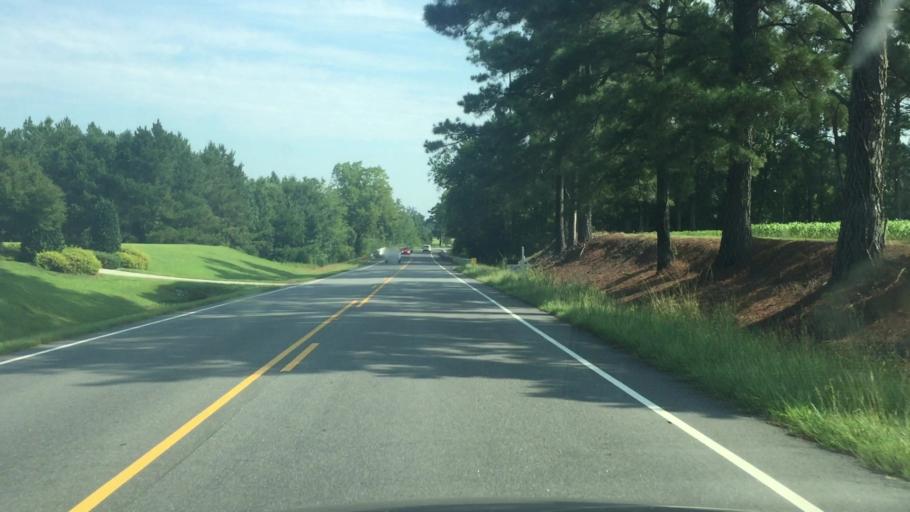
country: US
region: North Carolina
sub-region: Columbus County
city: Chadbourn
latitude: 34.2535
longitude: -78.8185
